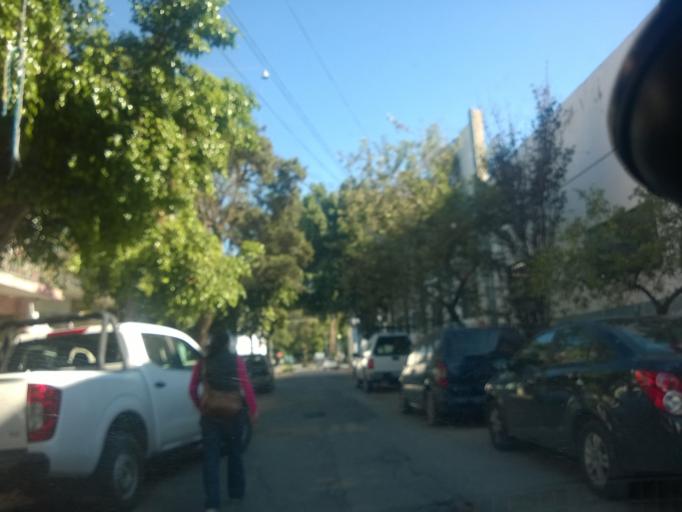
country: MX
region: Guanajuato
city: Leon
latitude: 21.1304
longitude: -101.6895
